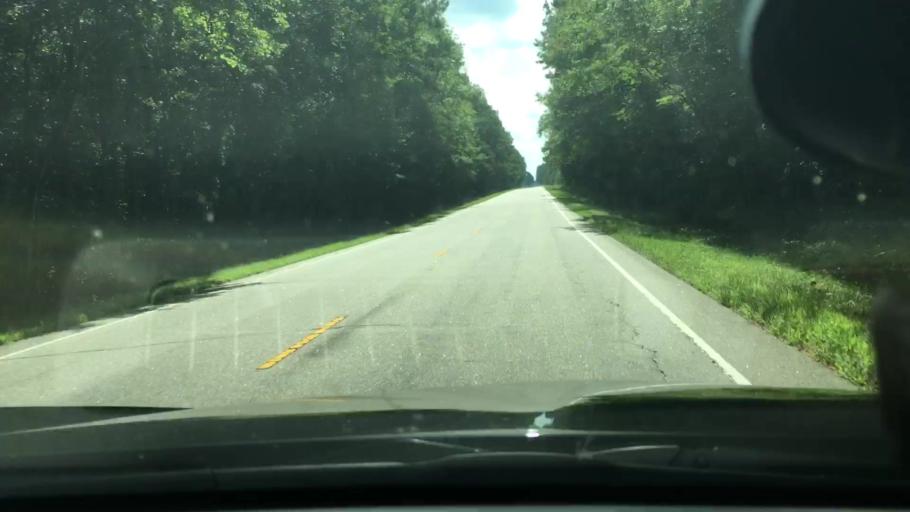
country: US
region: North Carolina
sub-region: Edgecombe County
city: Pinetops
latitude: 35.7670
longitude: -77.5659
